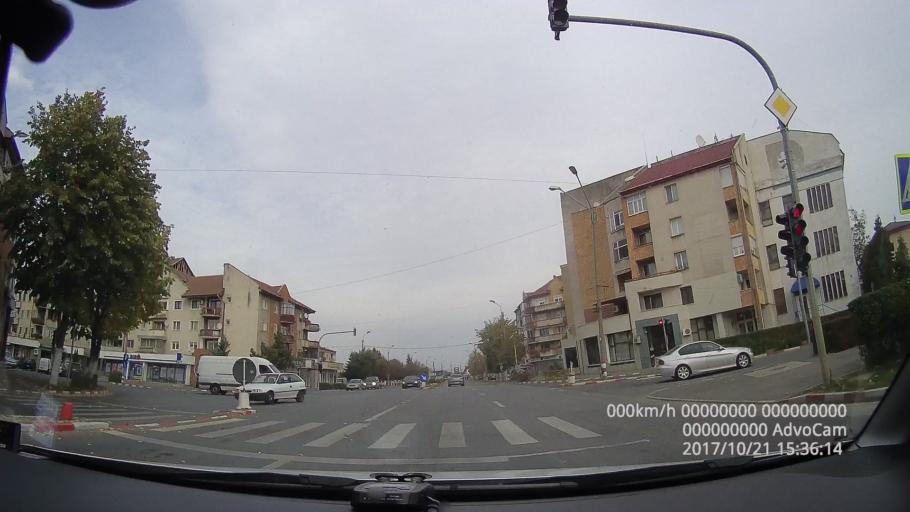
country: RO
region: Hunedoara
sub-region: Comuna Vetel
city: Vetel
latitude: 45.9189
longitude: 22.8458
